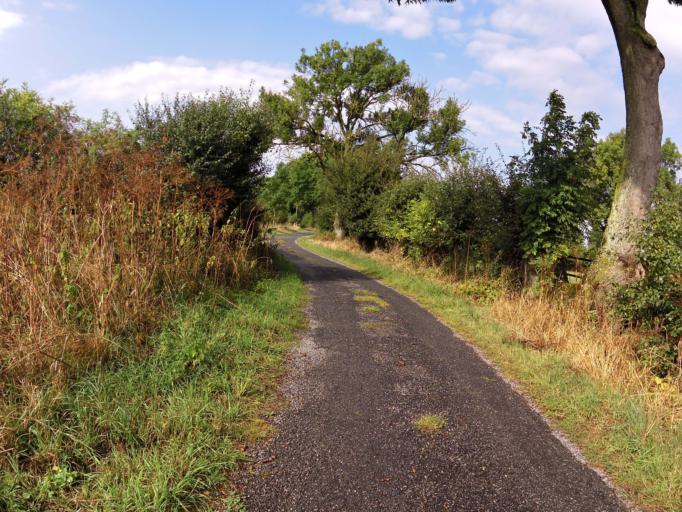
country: DE
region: Lower Saxony
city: Marklohe
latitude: 52.6608
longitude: 9.1822
